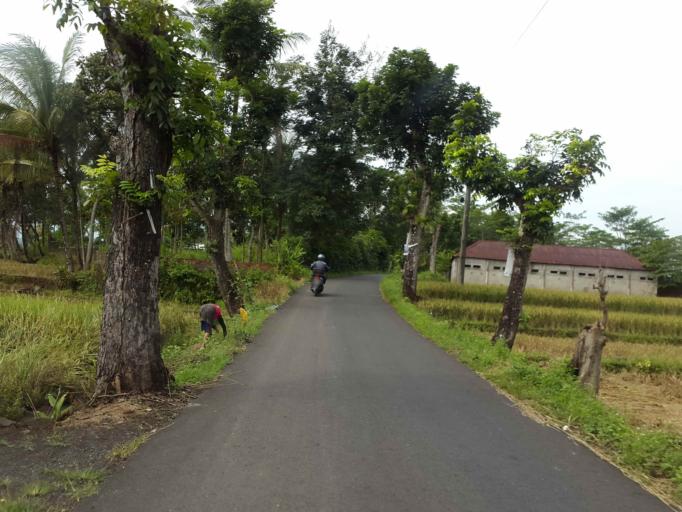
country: ID
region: Central Java
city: Randudongkal
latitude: -7.0501
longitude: 109.3310
